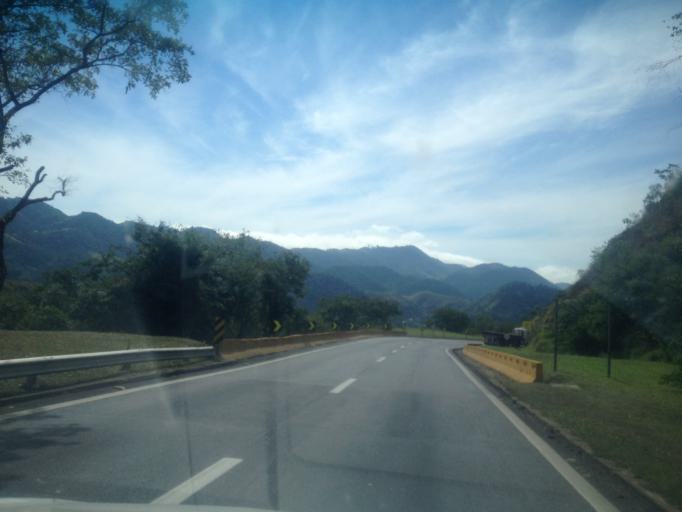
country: BR
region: Rio de Janeiro
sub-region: Pirai
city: Pirai
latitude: -22.6718
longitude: -43.8318
